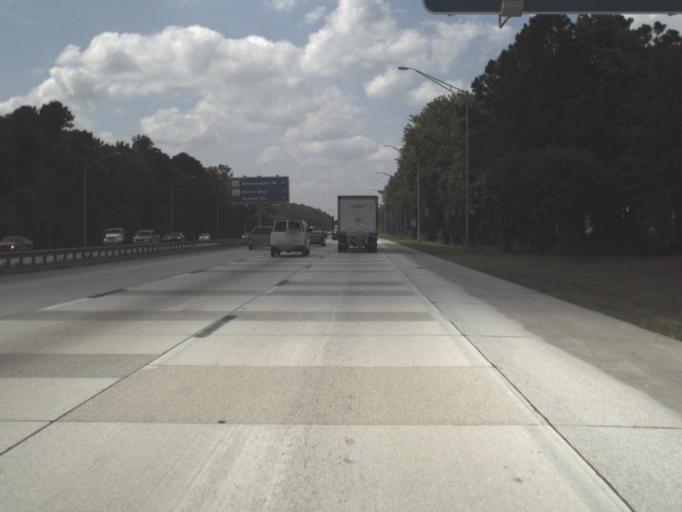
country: US
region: Florida
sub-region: Saint Johns County
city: Fruit Cove
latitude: 30.2056
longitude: -81.5611
